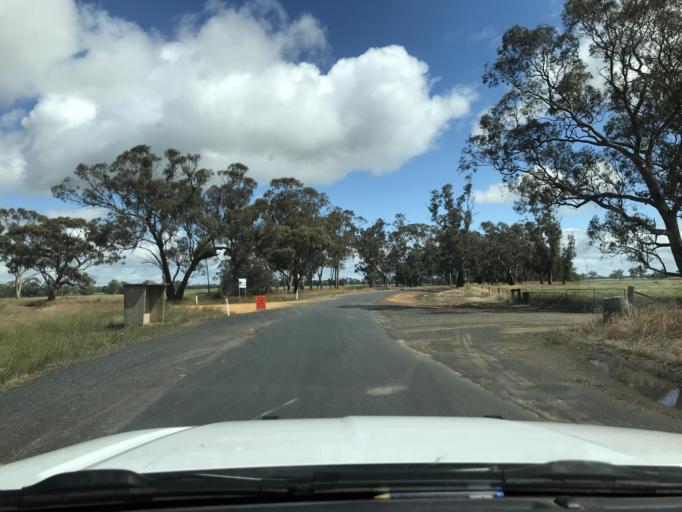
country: AU
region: Victoria
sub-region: Horsham
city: Horsham
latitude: -36.8061
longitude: 141.4783
